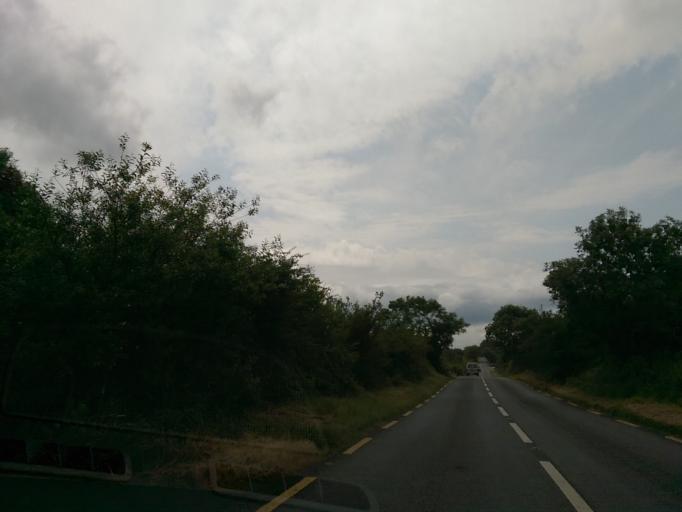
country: IE
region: Munster
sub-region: An Clar
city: Kilrush
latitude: 52.6487
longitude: -9.4618
